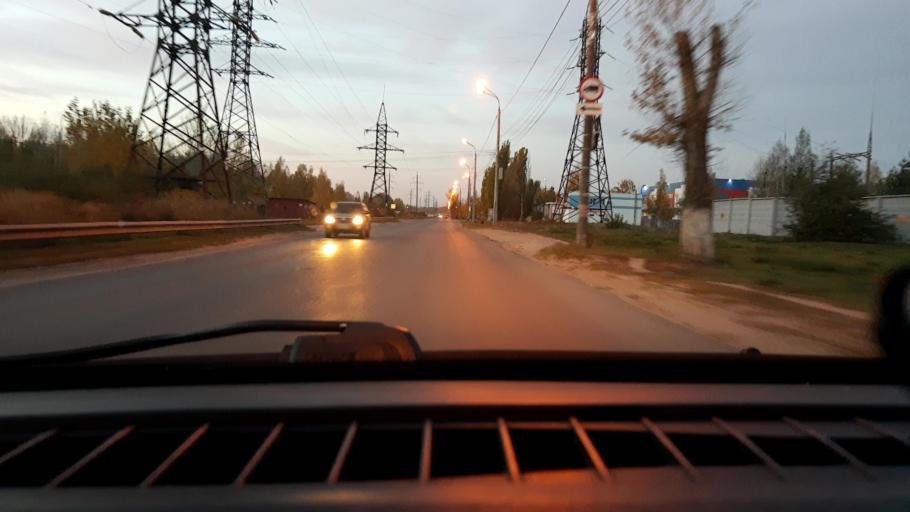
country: RU
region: Nizjnij Novgorod
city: Gorbatovka
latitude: 56.3708
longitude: 43.7984
